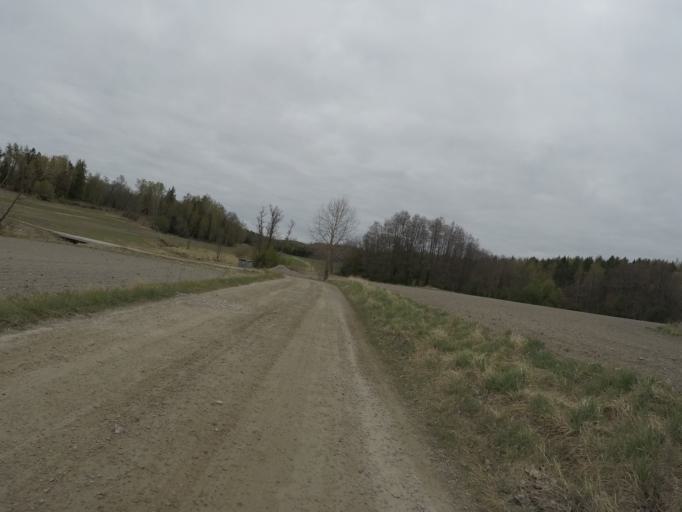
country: SE
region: Soedermanland
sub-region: Eskilstuna Kommun
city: Kvicksund
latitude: 59.4048
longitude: 16.2481
